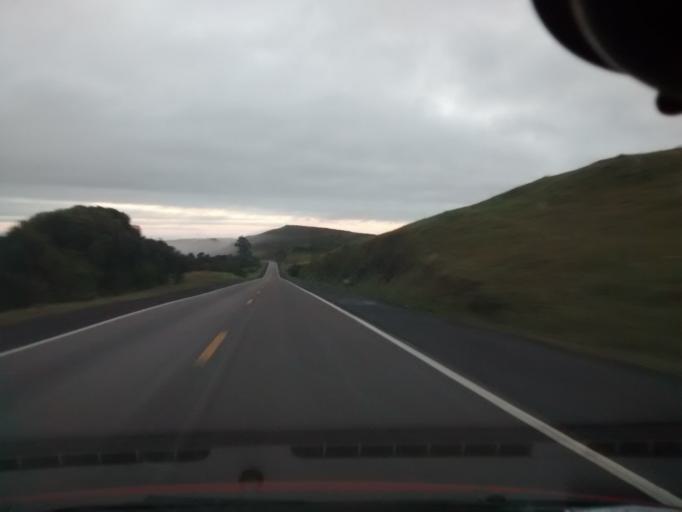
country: BR
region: Rio Grande do Sul
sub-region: Vacaria
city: Estrela
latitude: -28.1738
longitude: -50.6909
